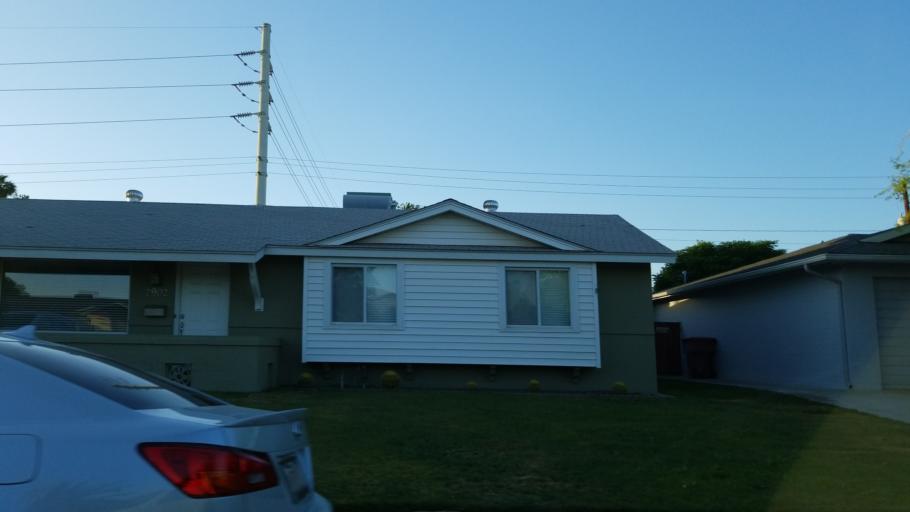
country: US
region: Arizona
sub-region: Maricopa County
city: Scottsdale
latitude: 33.4727
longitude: -111.9109
